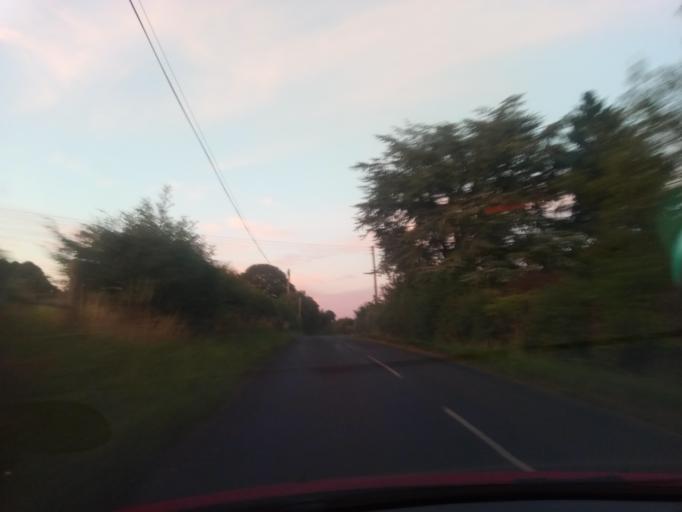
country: GB
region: England
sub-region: Northumberland
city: Bardon Mill
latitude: 54.9774
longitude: -2.2390
